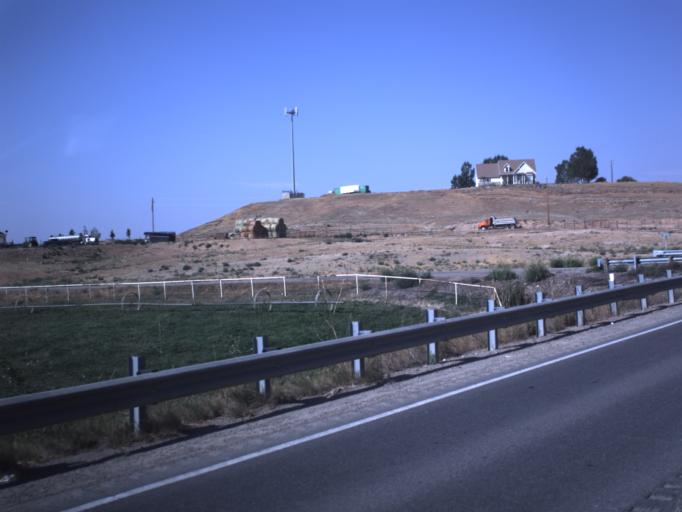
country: US
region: Utah
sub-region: Uintah County
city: Naples
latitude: 40.3693
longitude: -109.3841
